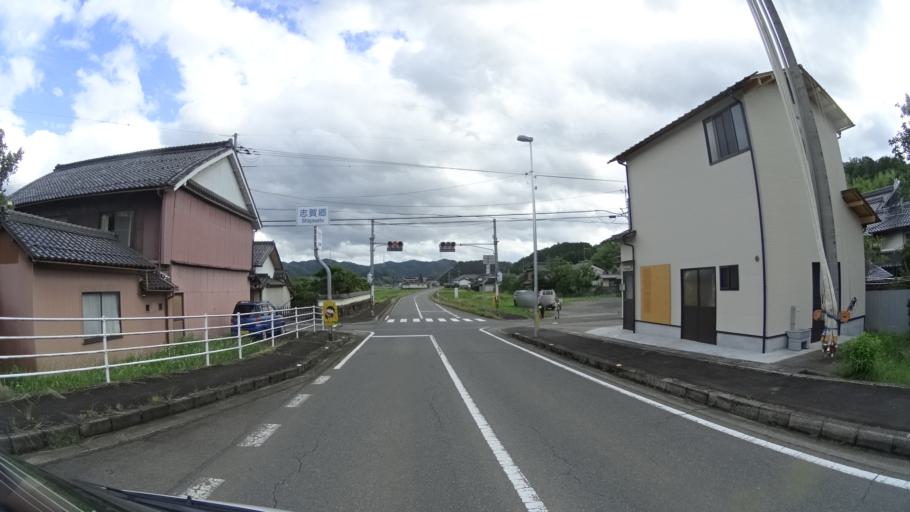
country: JP
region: Kyoto
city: Ayabe
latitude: 35.3682
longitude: 135.2401
